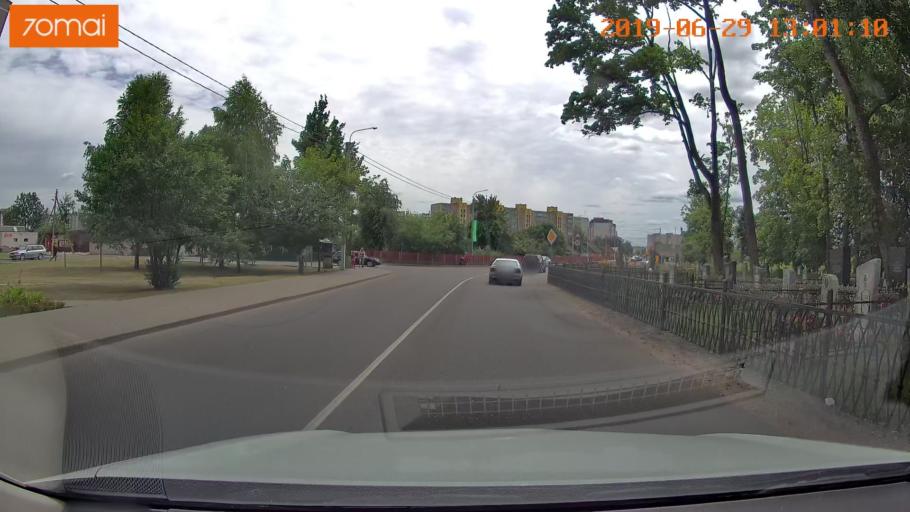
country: BY
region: Minsk
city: Slutsk
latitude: 53.0398
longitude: 27.5594
